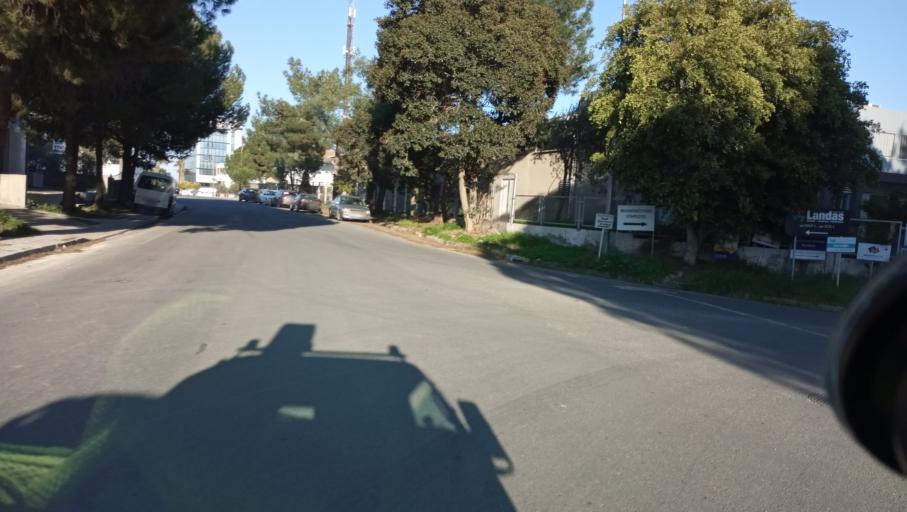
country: CY
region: Lefkosia
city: Nicosia
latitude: 35.1262
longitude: 33.3591
